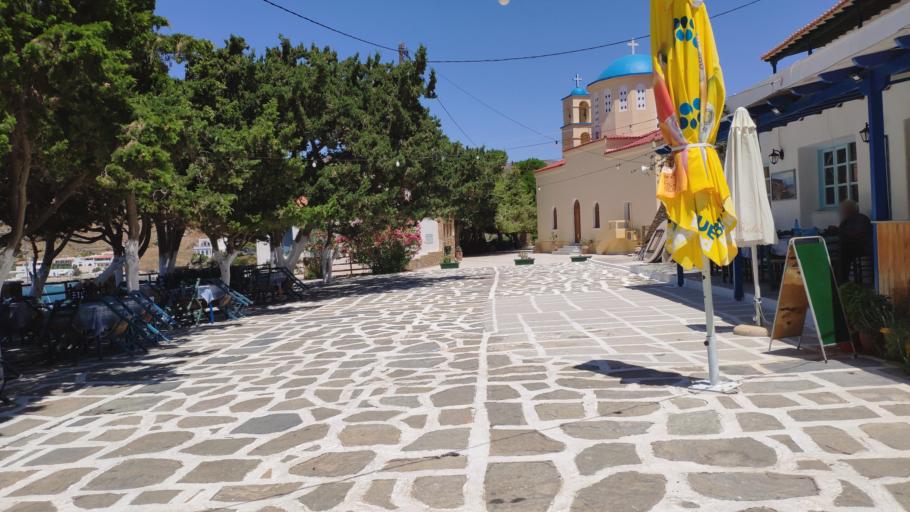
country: GR
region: South Aegean
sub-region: Nomos Kykladon
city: Kythnos
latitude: 37.3443
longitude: 24.4363
